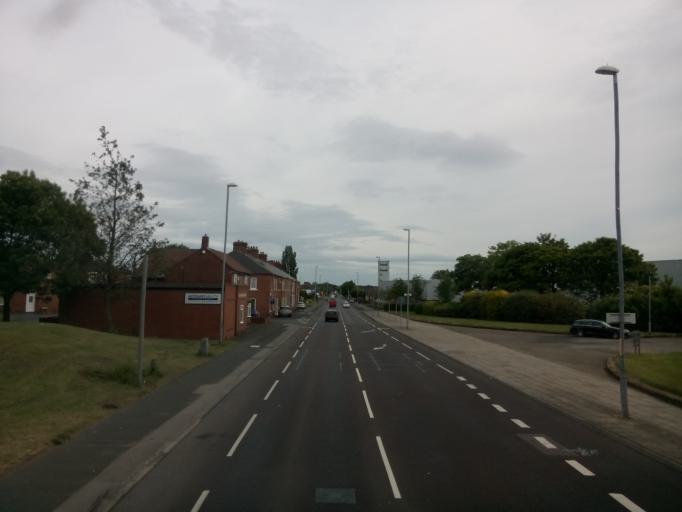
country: GB
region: England
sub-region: County Durham
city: Chester-le-Street
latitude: 54.8911
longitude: -1.5768
